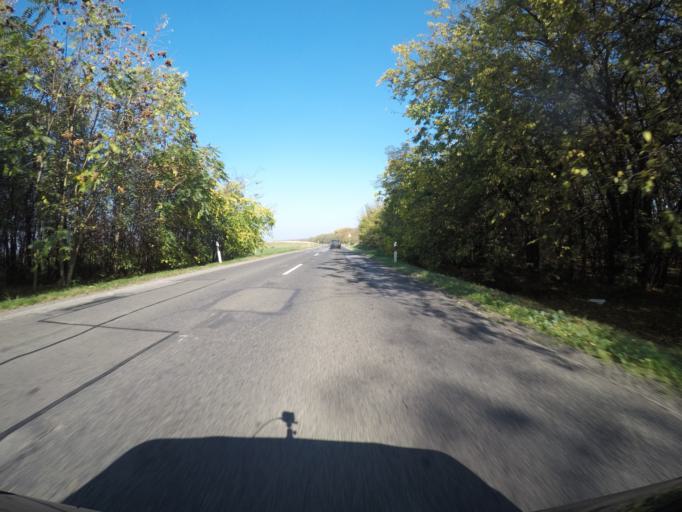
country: HU
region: Tolna
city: Szedres
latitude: 46.4594
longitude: 18.6879
